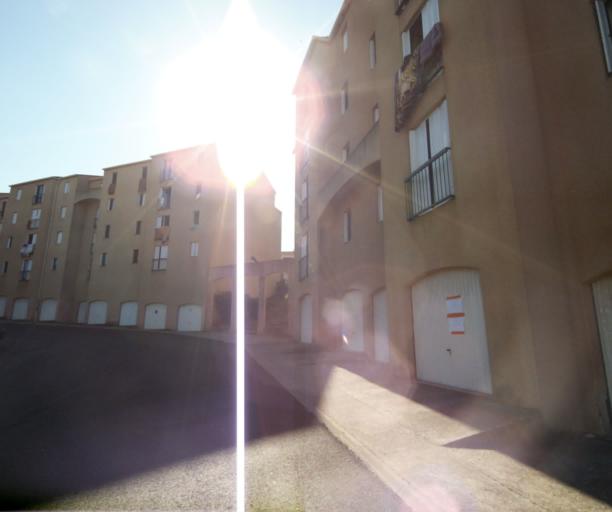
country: FR
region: Corsica
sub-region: Departement de la Corse-du-Sud
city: Propriano
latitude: 41.6681
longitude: 8.8985
